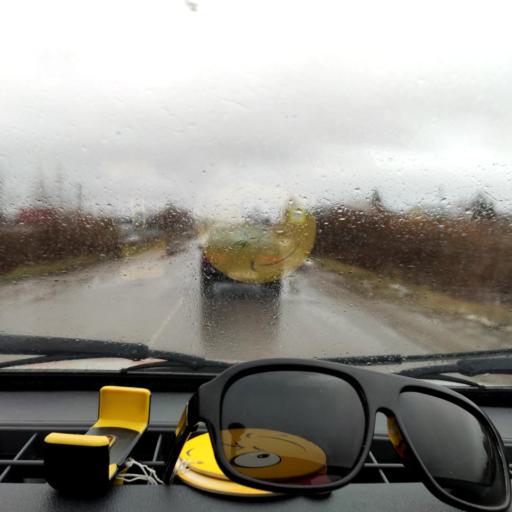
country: RU
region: Bashkortostan
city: Iglino
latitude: 54.8767
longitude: 56.5598
